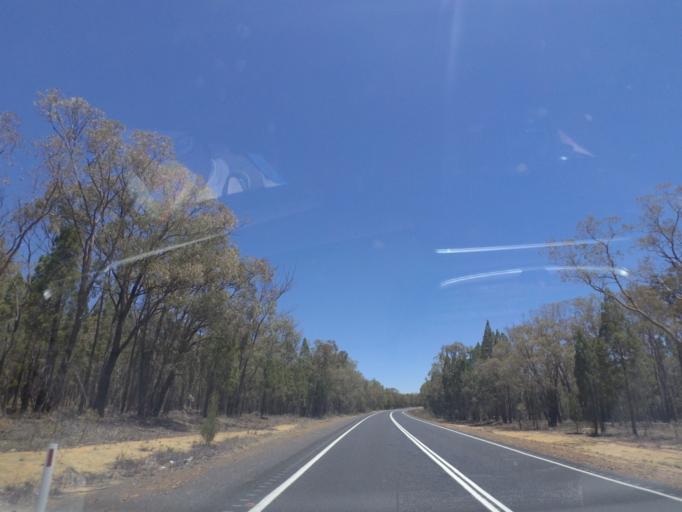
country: AU
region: New South Wales
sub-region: Warrumbungle Shire
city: Coonabarabran
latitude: -31.1944
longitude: 149.3518
